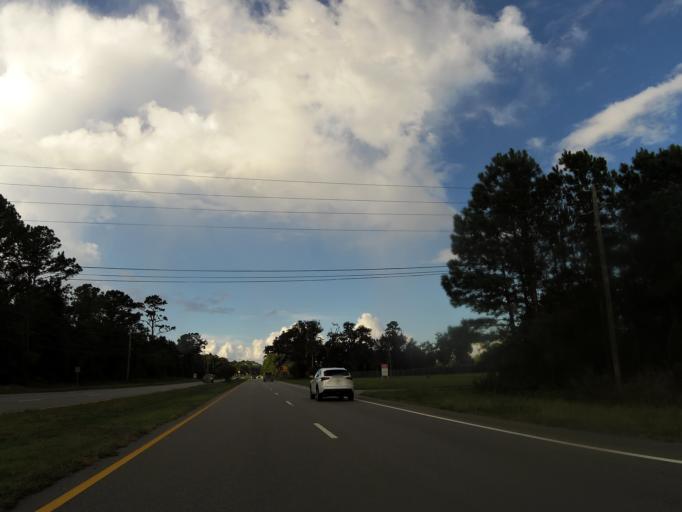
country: US
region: Georgia
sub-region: Glynn County
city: Country Club Estates
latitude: 31.2056
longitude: -81.4671
